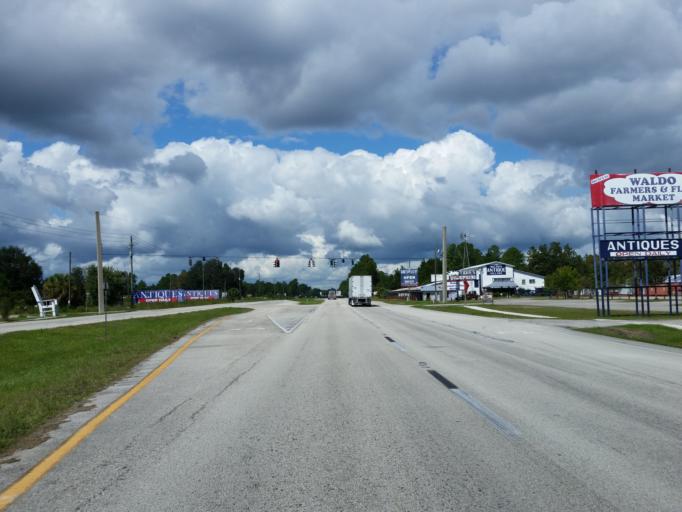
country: US
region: Florida
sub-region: Alachua County
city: Waldo
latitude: 29.8172
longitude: -82.1676
